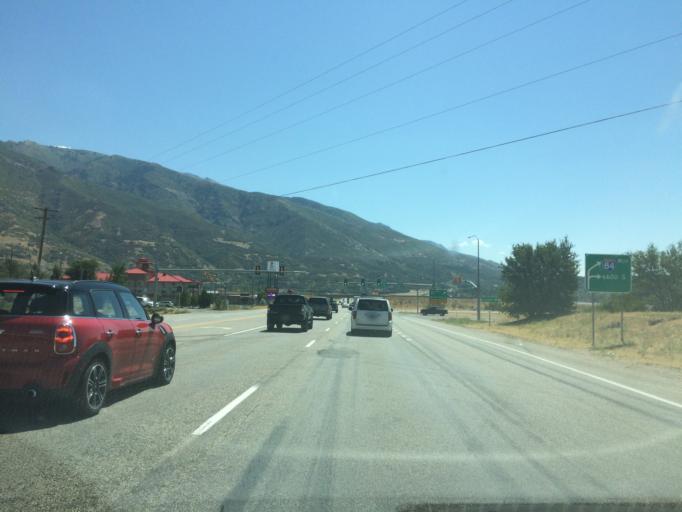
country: US
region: Utah
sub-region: Weber County
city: Uintah
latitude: 41.1410
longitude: -111.9165
